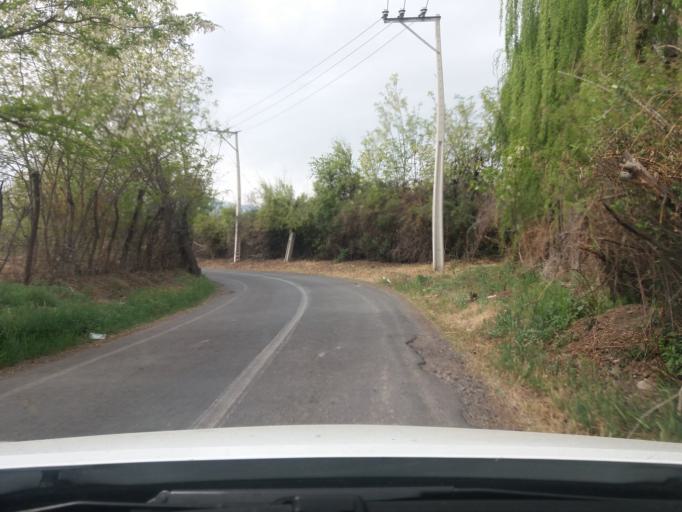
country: CL
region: Valparaiso
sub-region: Provincia de Los Andes
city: Los Andes
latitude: -32.8282
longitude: -70.6355
